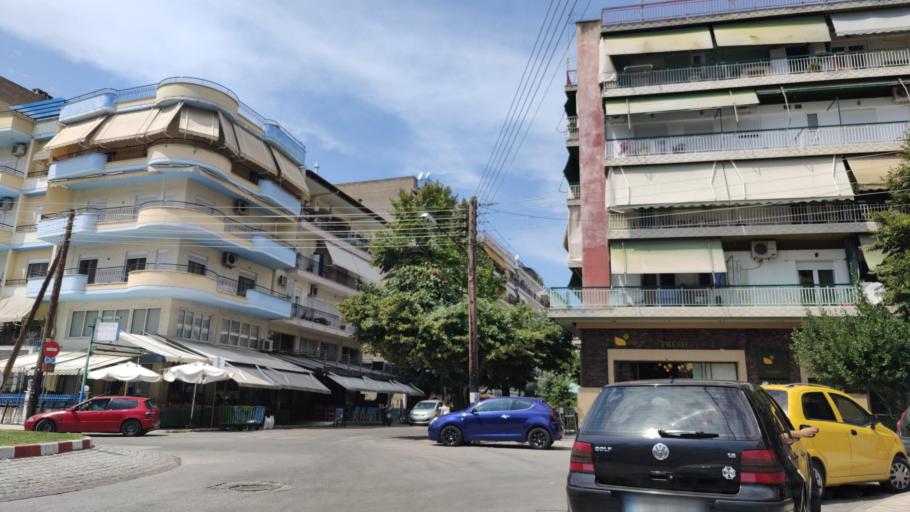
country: GR
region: Central Macedonia
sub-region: Nomos Serron
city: Serres
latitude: 41.0865
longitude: 23.5417
